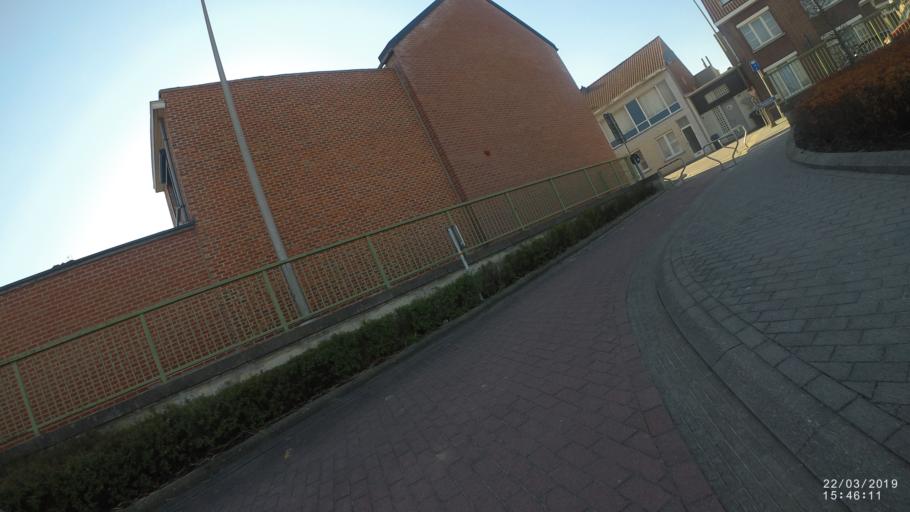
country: BE
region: Flanders
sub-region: Provincie Limburg
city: Bilzen
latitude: 50.8670
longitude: 5.5086
